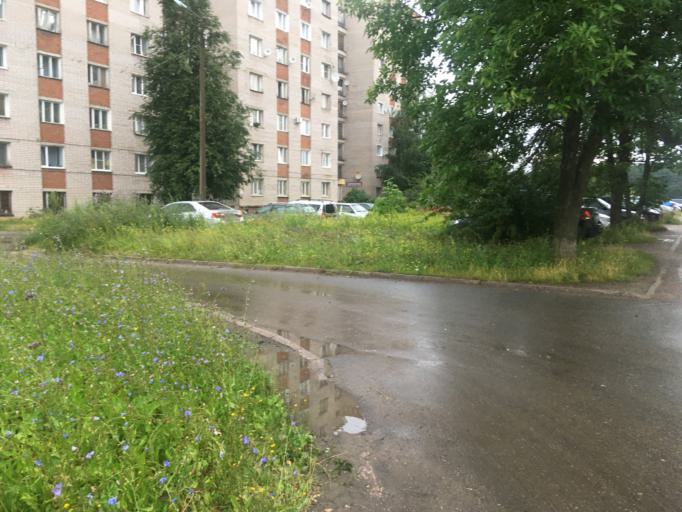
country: RU
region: Ivanovo
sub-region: Gorod Ivanovo
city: Ivanovo
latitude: 56.9506
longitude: 40.9814
